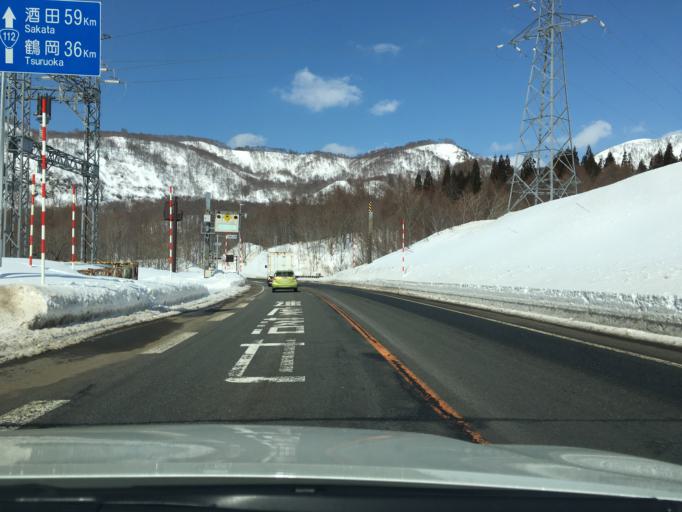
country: JP
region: Yamagata
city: Tsuruoka
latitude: 38.5292
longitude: 139.9506
